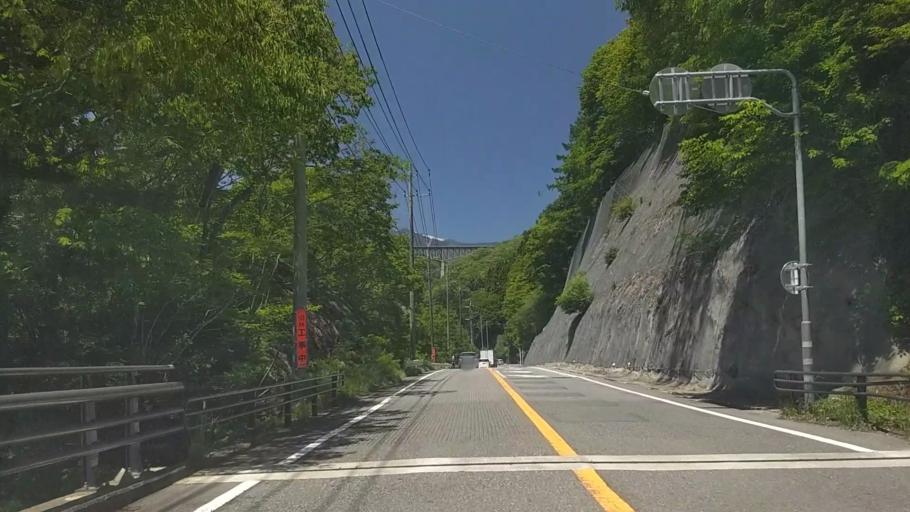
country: JP
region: Yamanashi
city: Nirasaki
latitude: 35.8826
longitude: 138.4288
